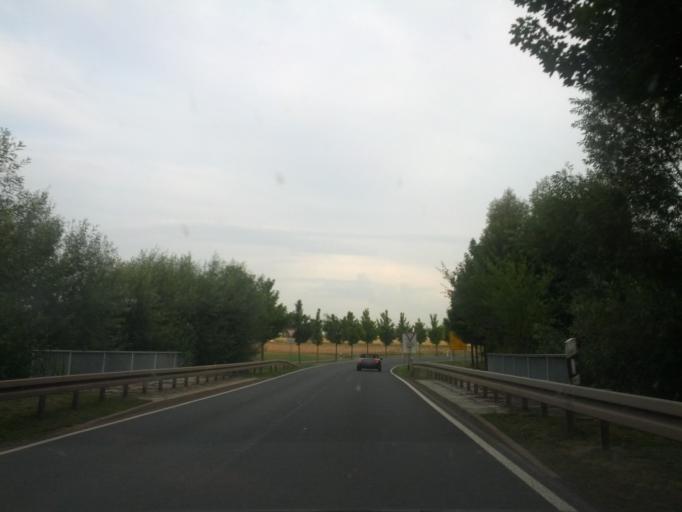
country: DE
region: Thuringia
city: Gotha
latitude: 50.9312
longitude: 10.6820
